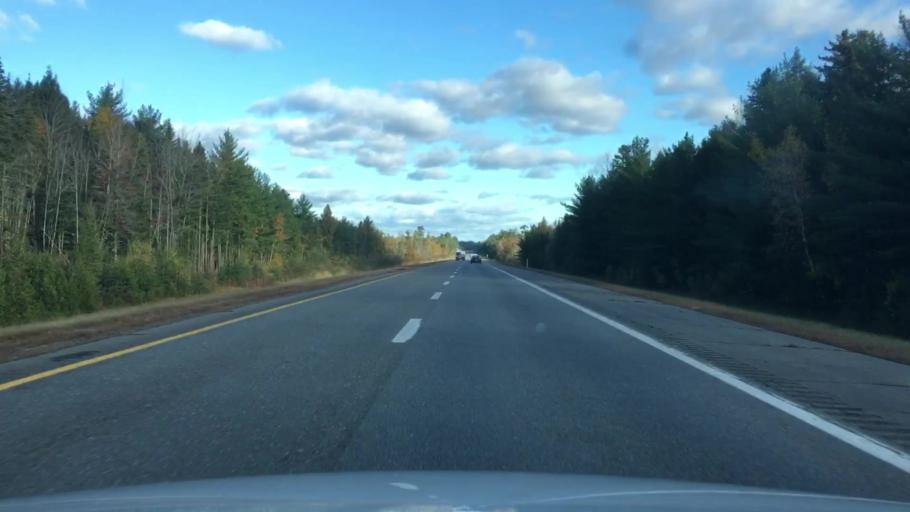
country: US
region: Maine
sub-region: Penobscot County
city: Greenbush
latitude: 45.1273
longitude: -68.6956
